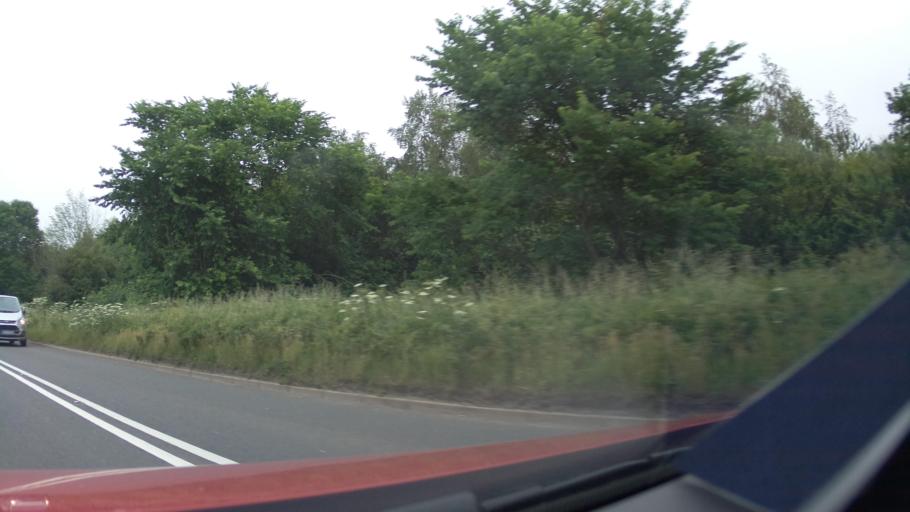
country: GB
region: England
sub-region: Derbyshire
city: Netherseal
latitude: 52.7229
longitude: -1.5596
